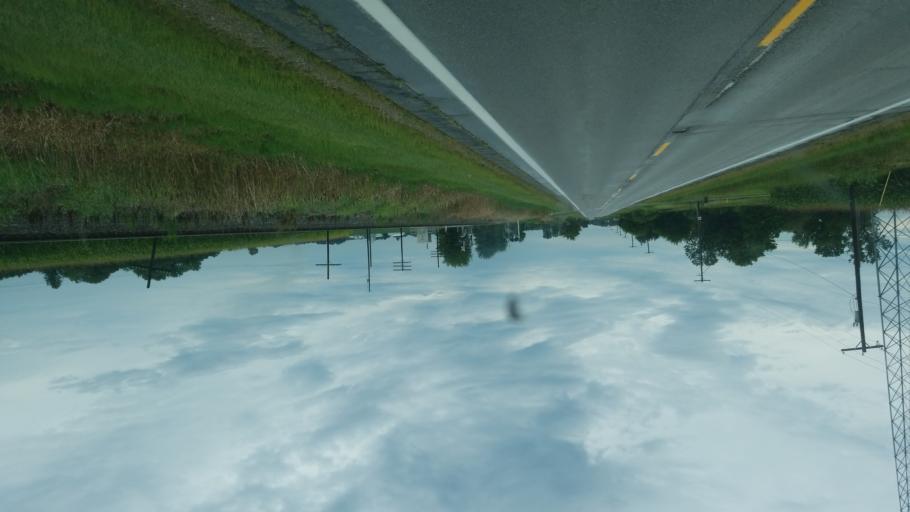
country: US
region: Ohio
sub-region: Delaware County
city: Ashley
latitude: 40.3846
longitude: -82.9714
